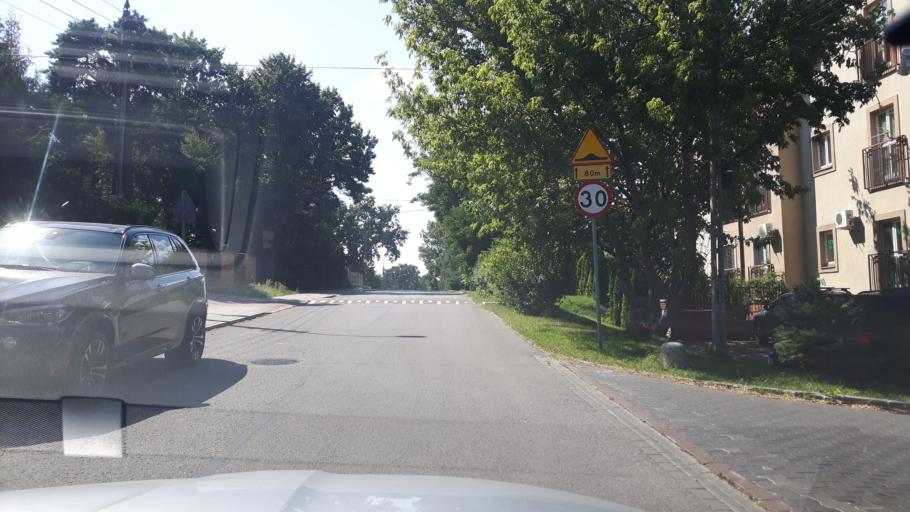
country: PL
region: Masovian Voivodeship
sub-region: Warszawa
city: Rembertow
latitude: 52.2447
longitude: 21.1851
